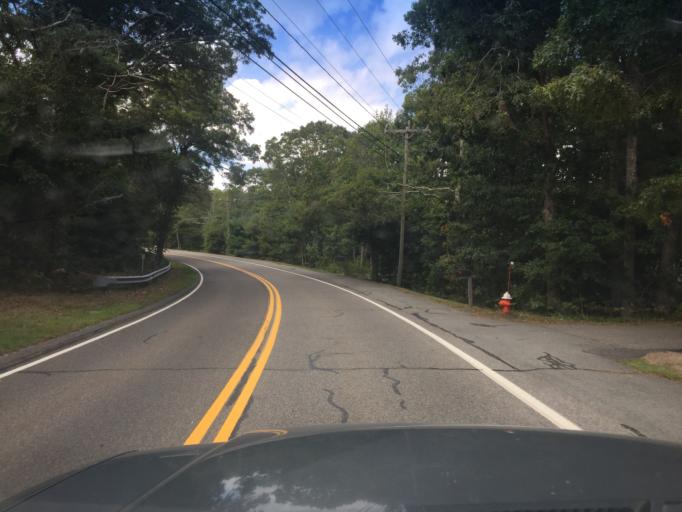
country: US
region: Massachusetts
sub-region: Barnstable County
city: Monument Beach
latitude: 41.7164
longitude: -70.5988
